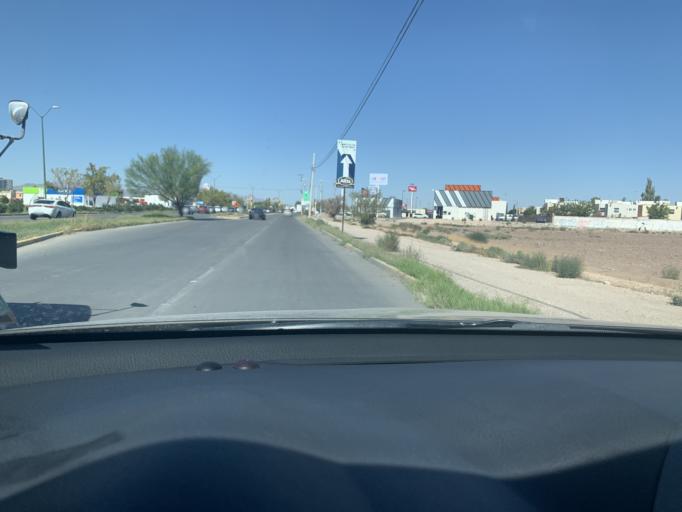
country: US
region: Texas
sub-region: El Paso County
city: Socorro
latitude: 31.6983
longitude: -106.3822
